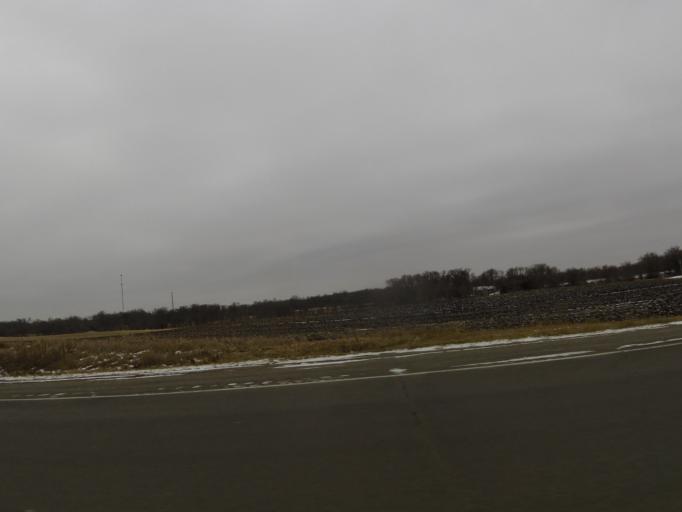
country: US
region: Minnesota
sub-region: Wright County
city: Delano
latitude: 45.0648
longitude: -93.8400
